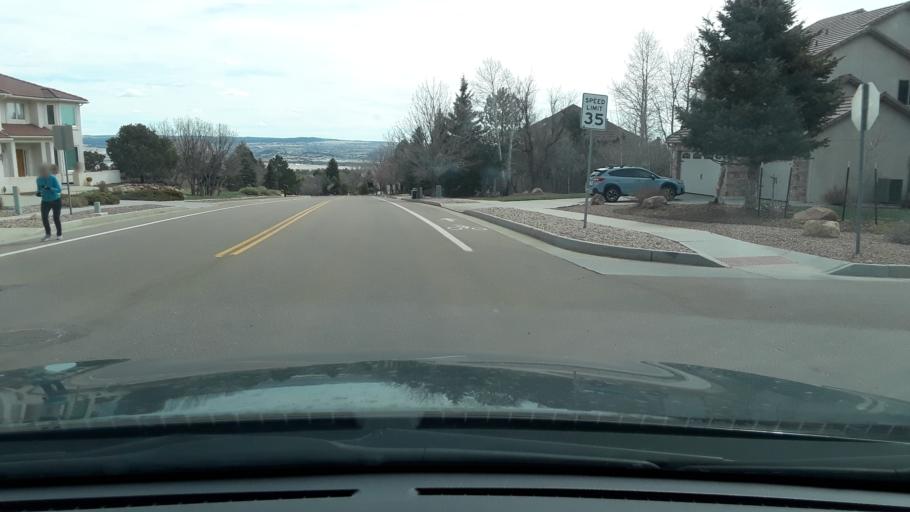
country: US
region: Colorado
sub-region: El Paso County
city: Air Force Academy
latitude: 38.9532
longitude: -104.8742
